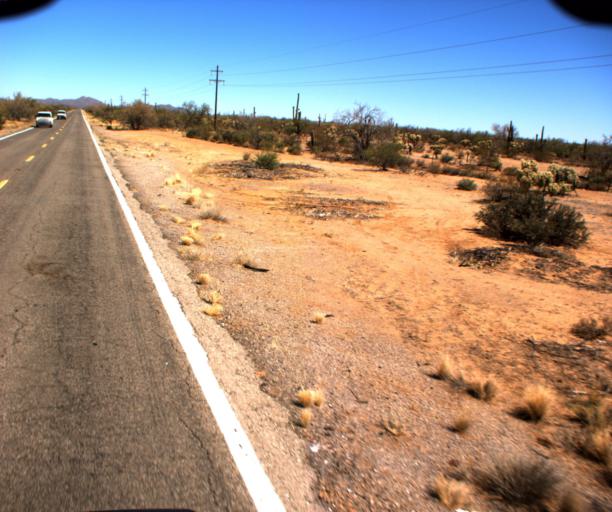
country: US
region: Arizona
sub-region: Pima County
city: Sells
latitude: 32.1019
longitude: -112.0670
